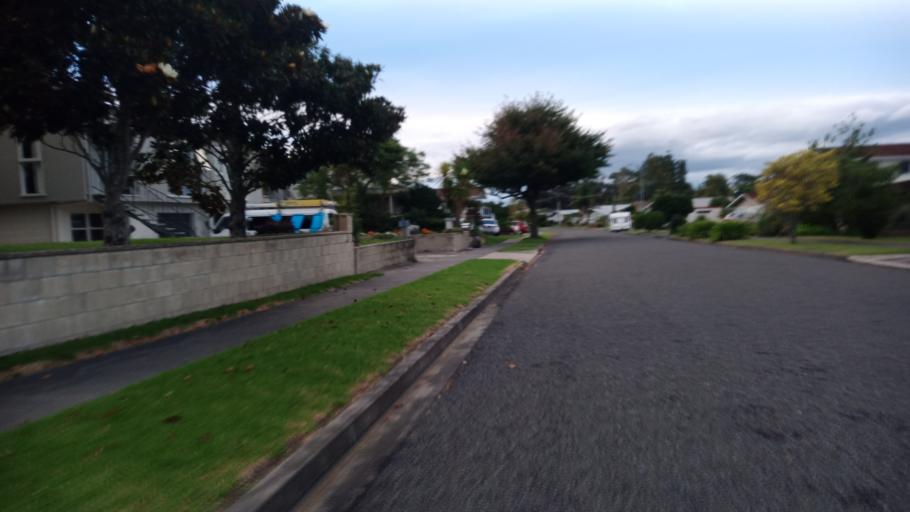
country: NZ
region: Gisborne
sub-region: Gisborne District
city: Gisborne
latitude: -38.6498
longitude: 178.0086
